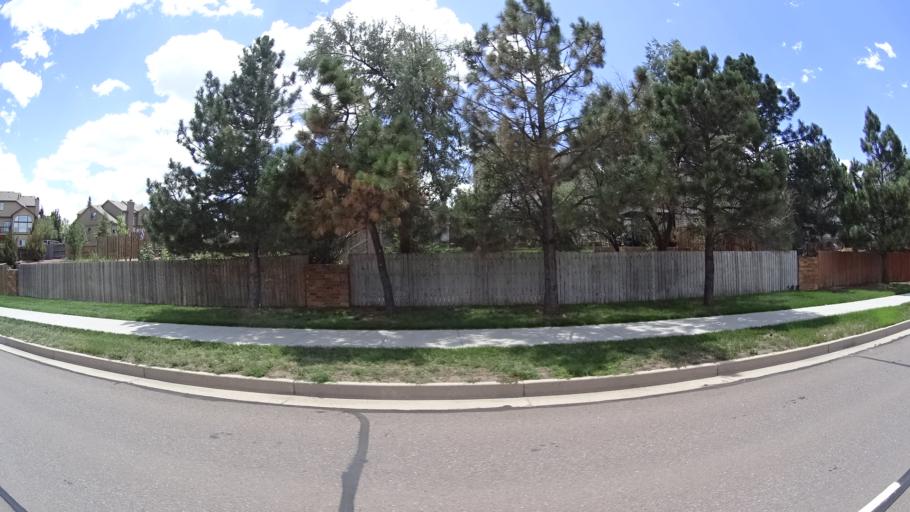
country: US
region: Colorado
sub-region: El Paso County
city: Black Forest
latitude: 38.9546
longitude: -104.7443
